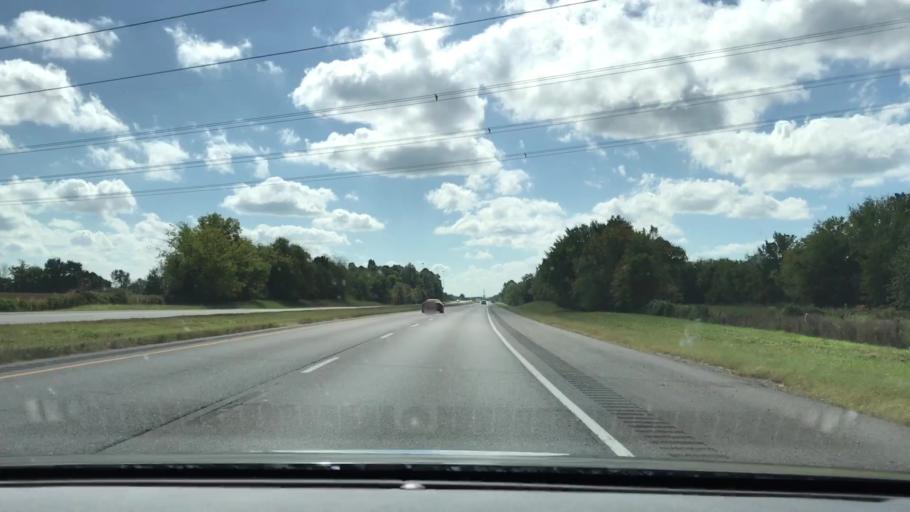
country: US
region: Kentucky
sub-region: McCracken County
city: Reidland
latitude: 37.0026
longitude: -88.5070
